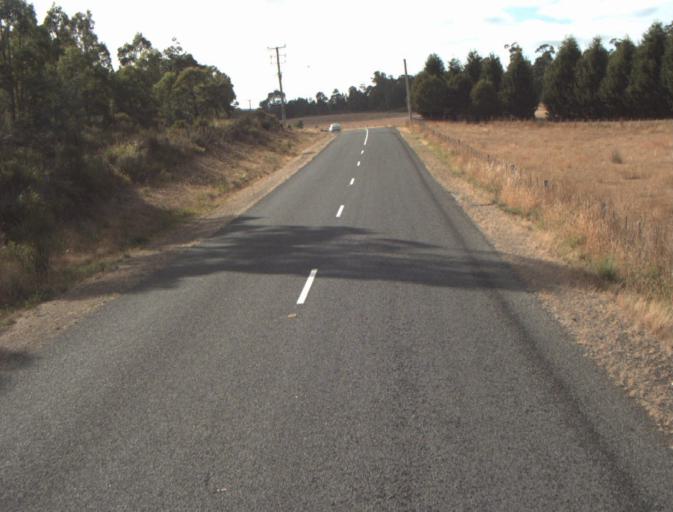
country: AU
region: Tasmania
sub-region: Dorset
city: Bridport
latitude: -41.1318
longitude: 147.2163
